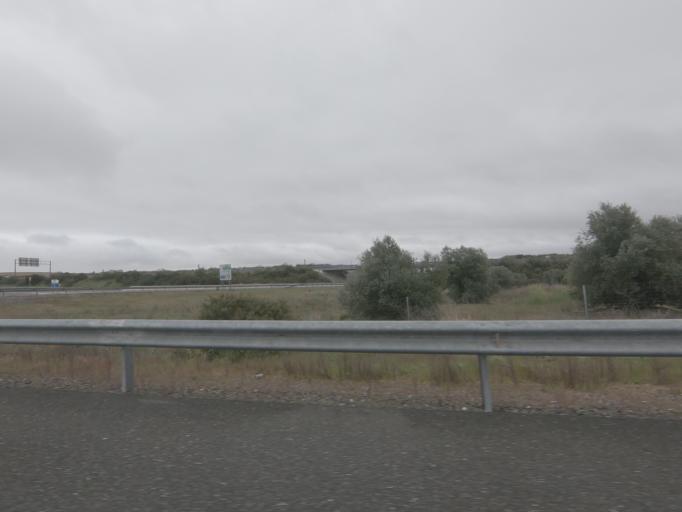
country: ES
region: Extremadura
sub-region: Provincia de Caceres
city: Casar de Caceres
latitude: 39.5379
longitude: -6.4091
